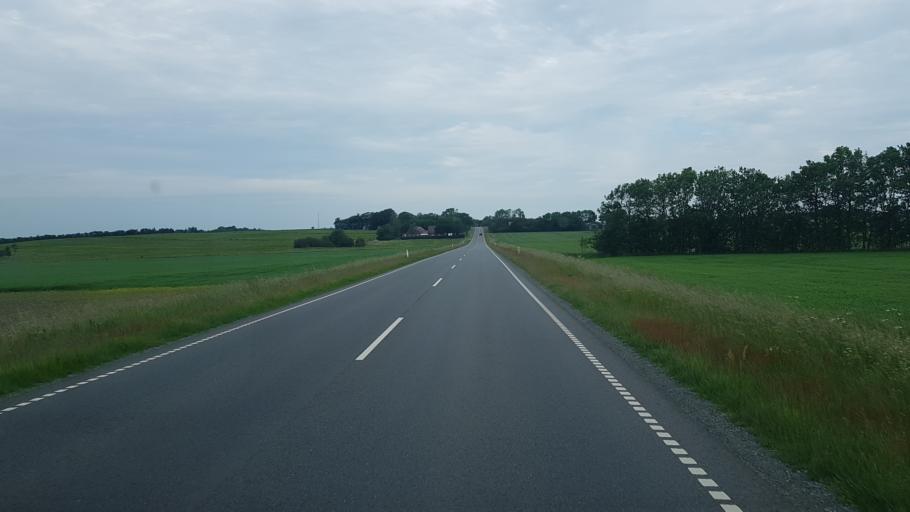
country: DK
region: South Denmark
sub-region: Vejen Kommune
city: Rodding
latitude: 55.4129
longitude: 9.0289
